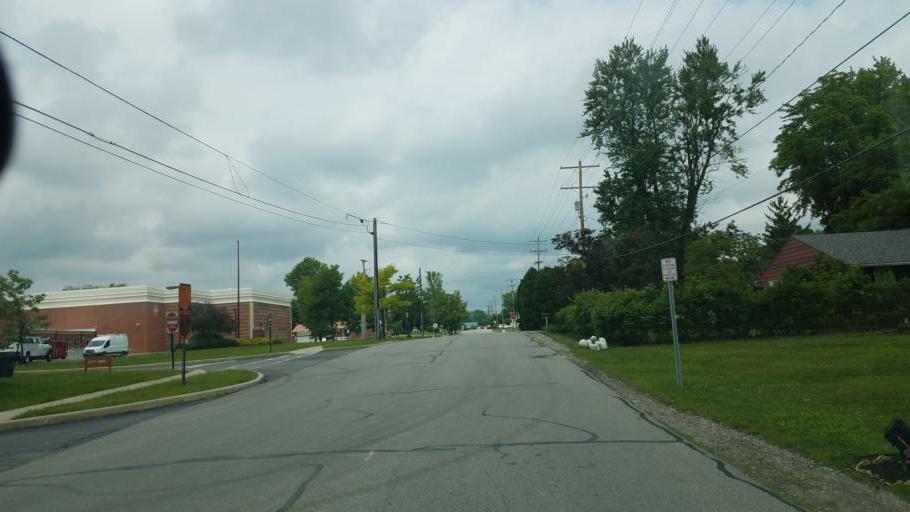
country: US
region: Ohio
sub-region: Delaware County
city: Delaware
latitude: 40.3101
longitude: -83.0782
